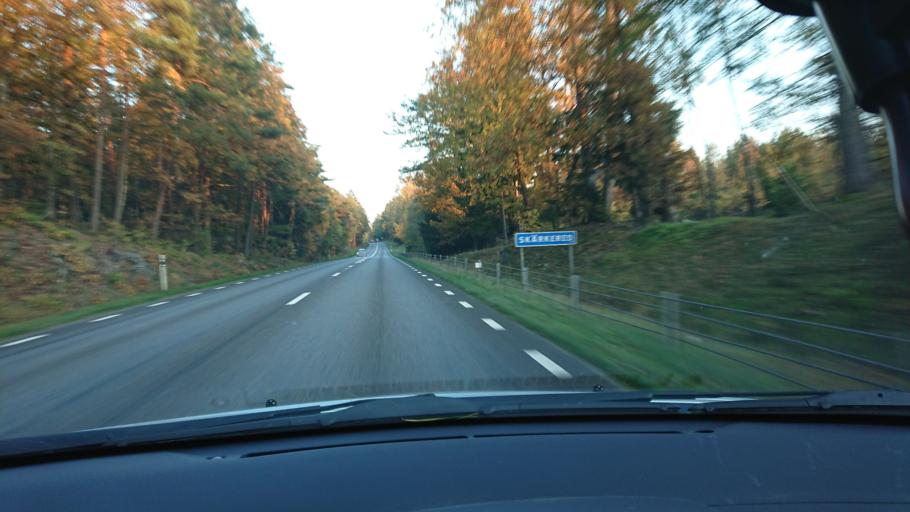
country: SE
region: Halland
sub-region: Halmstads Kommun
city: Oskarstrom
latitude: 56.7082
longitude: 13.0540
